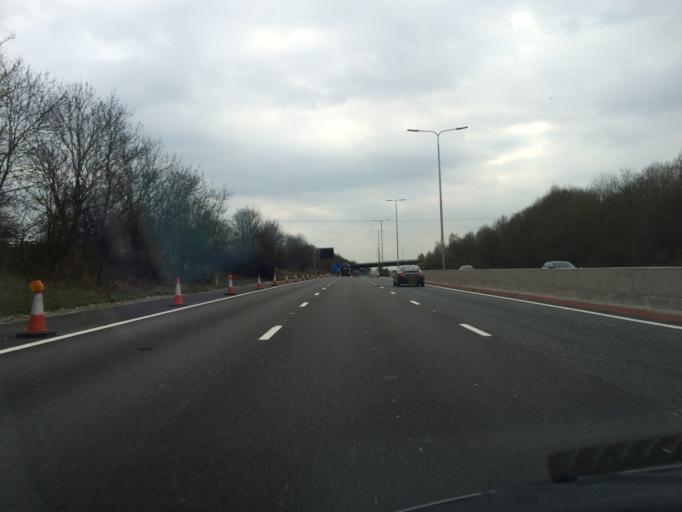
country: GB
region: England
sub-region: Wokingham
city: Shinfield
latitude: 51.4160
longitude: -0.9448
